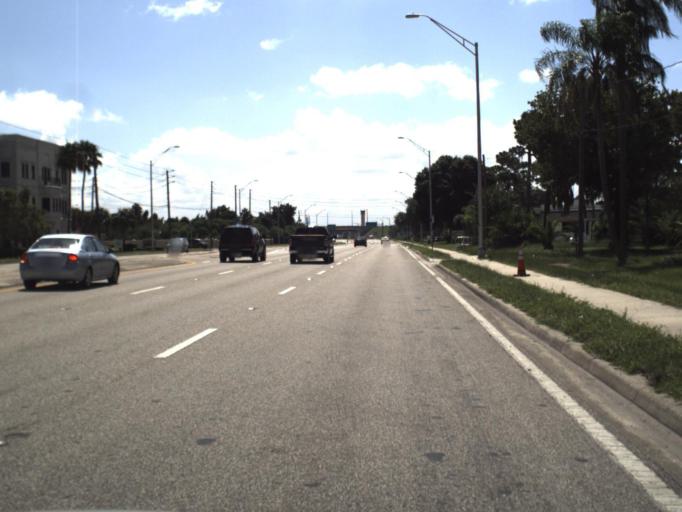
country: US
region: Florida
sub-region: Pinellas County
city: South Highpoint
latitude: 27.9140
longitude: -82.7066
